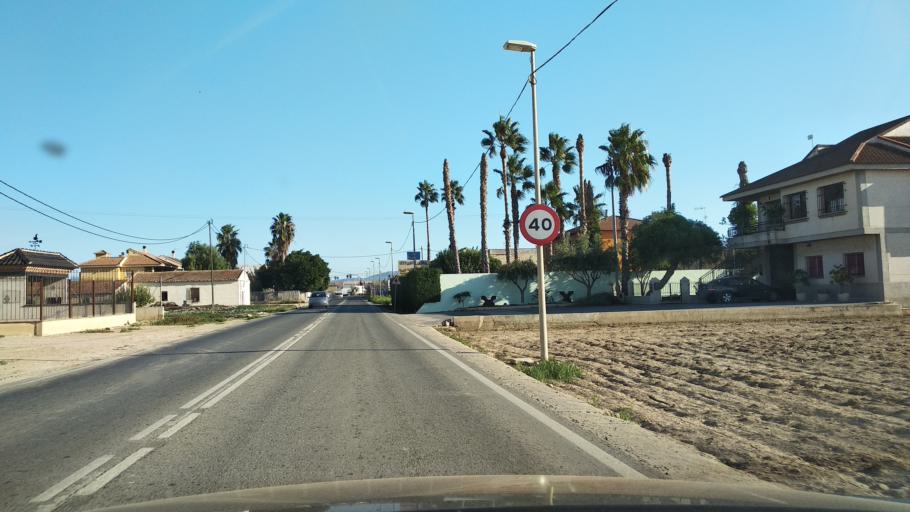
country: ES
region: Murcia
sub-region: Murcia
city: Santomera
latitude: 38.0413
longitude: -1.0494
